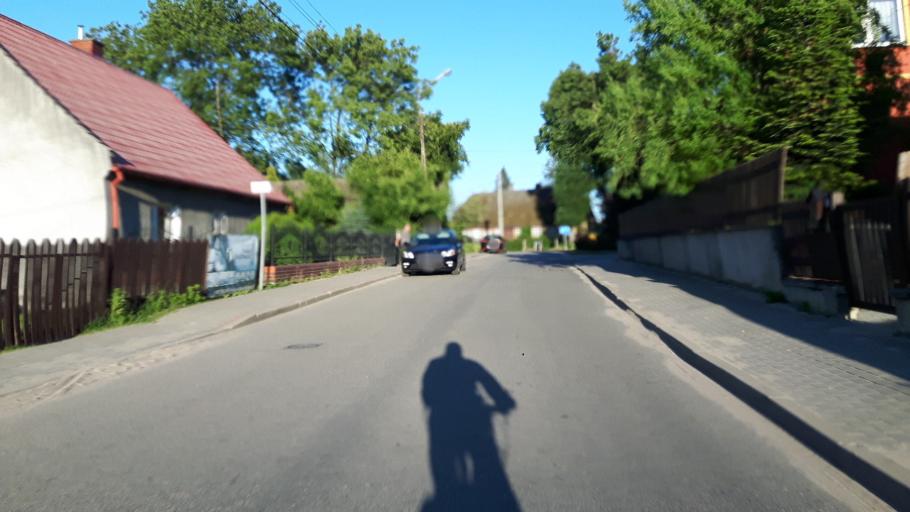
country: PL
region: Pomeranian Voivodeship
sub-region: Powiat pucki
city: Mosty
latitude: 54.6092
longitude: 18.5112
